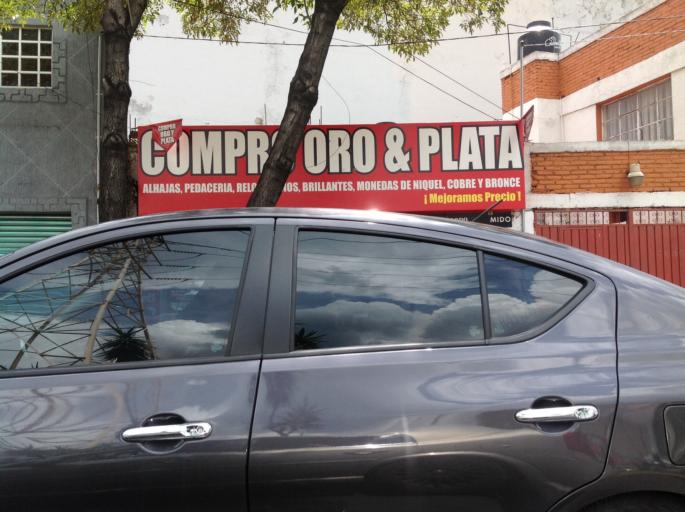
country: MX
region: Mexico City
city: Azcapotzalco
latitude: 19.4697
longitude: -99.1891
